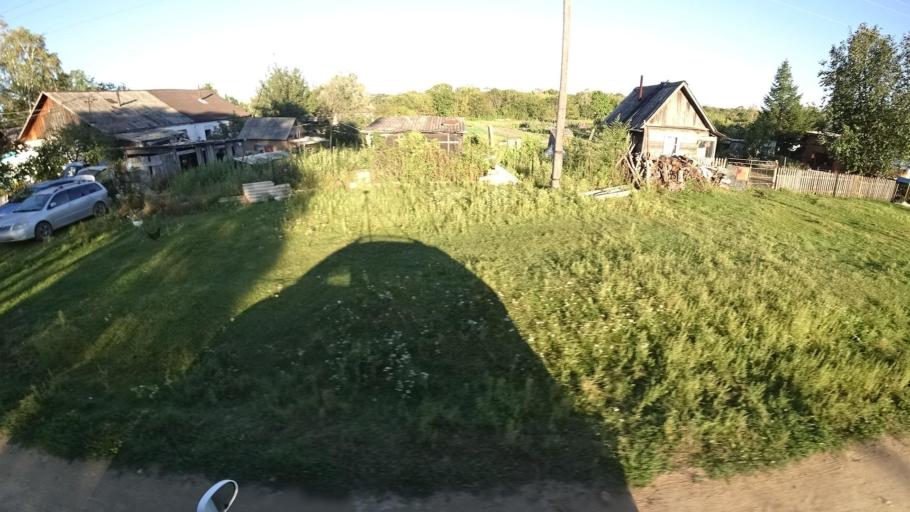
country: RU
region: Primorskiy
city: Kirovskiy
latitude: 44.8316
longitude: 133.5729
